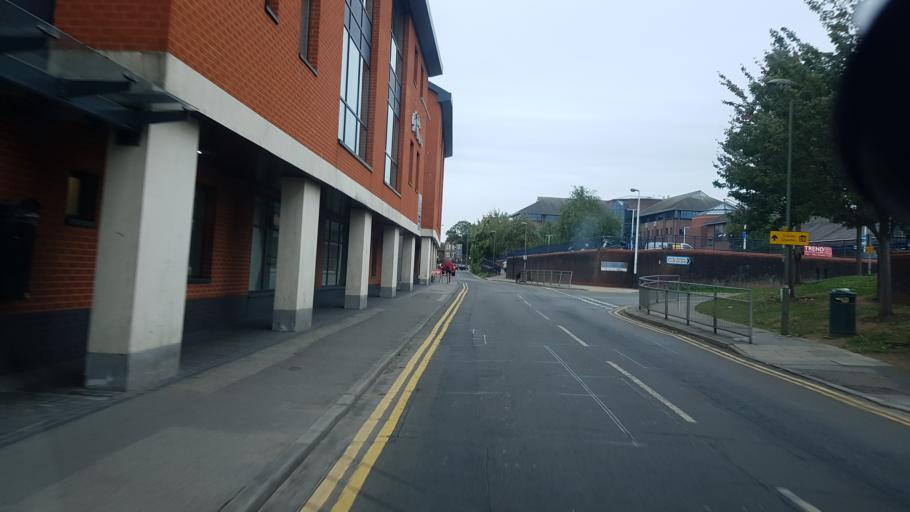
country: GB
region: England
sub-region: Surrey
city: Guildford
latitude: 51.2381
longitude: -0.5801
